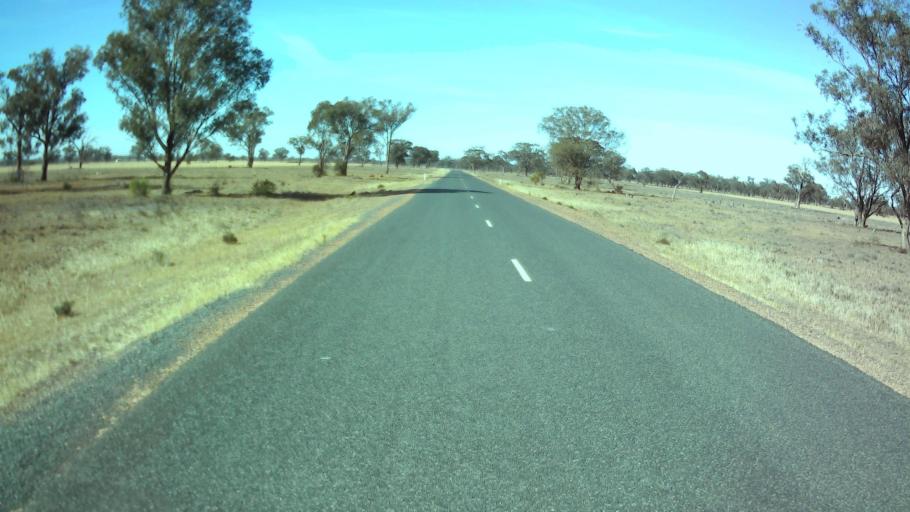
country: AU
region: New South Wales
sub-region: Weddin
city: Grenfell
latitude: -34.0747
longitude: 147.9008
